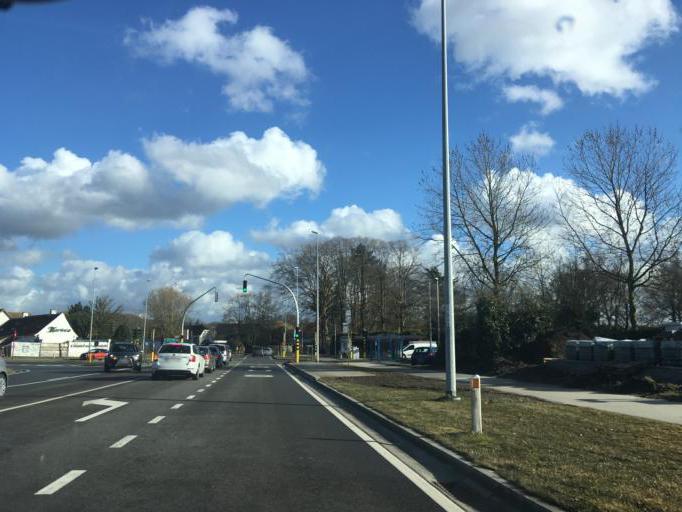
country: BE
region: Flanders
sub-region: Provincie Oost-Vlaanderen
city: Merelbeke
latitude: 51.0041
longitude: 3.7627
